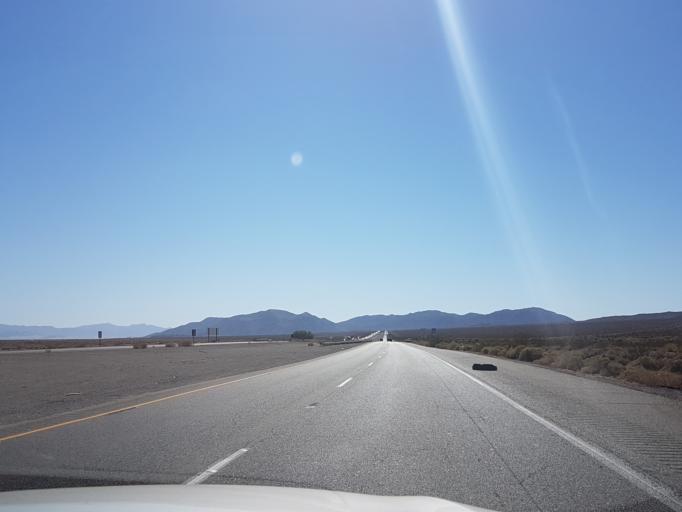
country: US
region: California
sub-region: San Bernardino County
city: Fort Irwin
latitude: 35.2507
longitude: -116.0914
